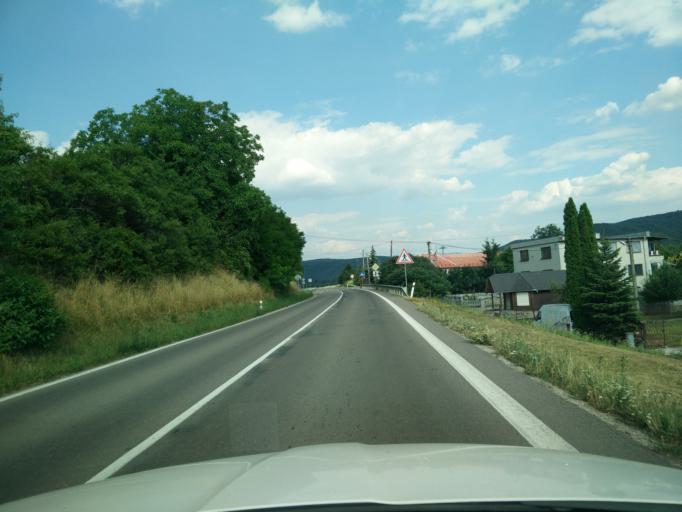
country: SK
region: Nitriansky
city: Partizanske
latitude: 48.7085
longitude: 18.4286
